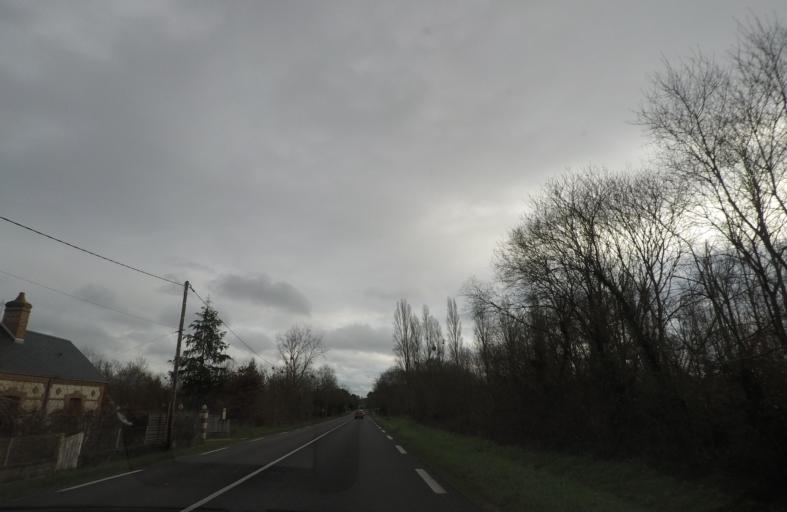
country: FR
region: Centre
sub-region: Departement du Loir-et-Cher
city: Mur-de-Sologne
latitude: 47.4067
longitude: 1.6177
